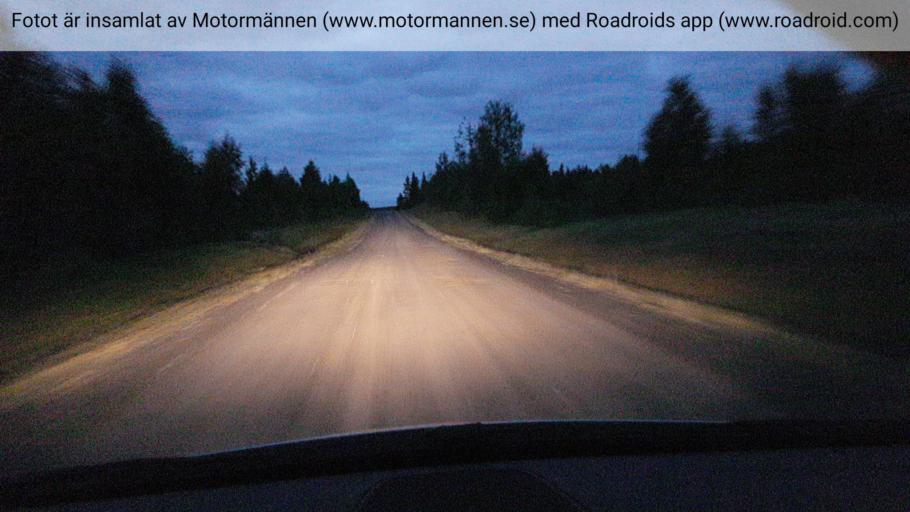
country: SE
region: Jaemtland
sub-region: Braecke Kommun
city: Braecke
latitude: 63.2551
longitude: 15.3714
